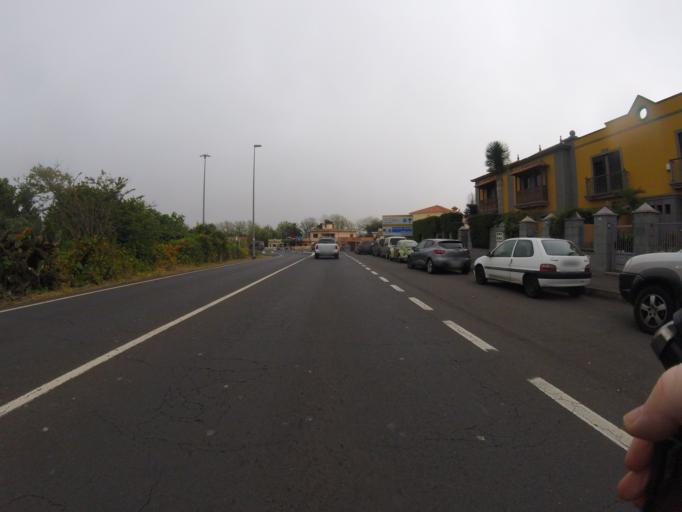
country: ES
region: Canary Islands
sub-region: Provincia de Santa Cruz de Tenerife
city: Tacoronte
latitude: 28.4920
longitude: -16.3726
